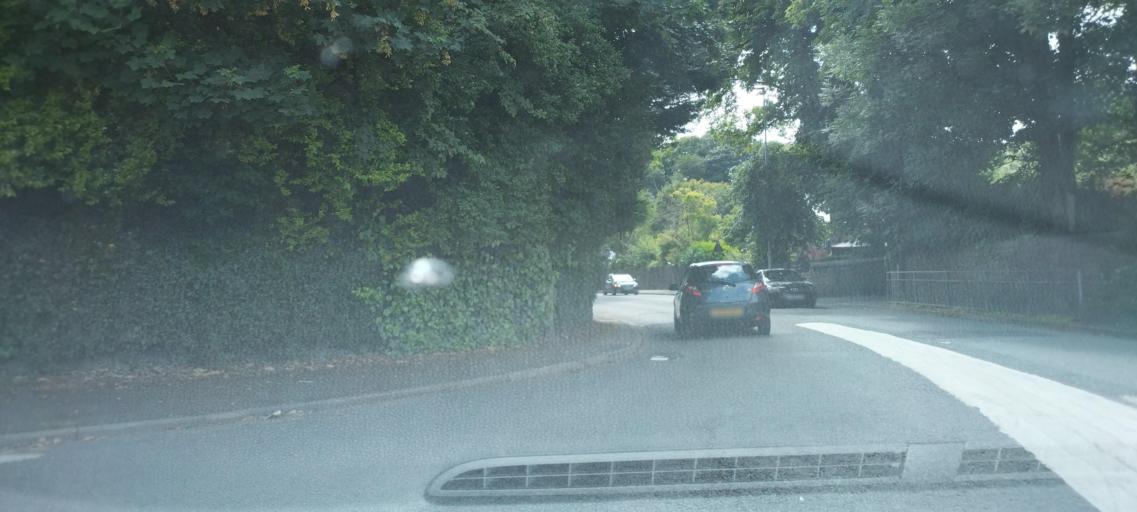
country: GB
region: England
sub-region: Blackburn with Darwen
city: Blackburn
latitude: 53.7263
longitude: -2.5393
